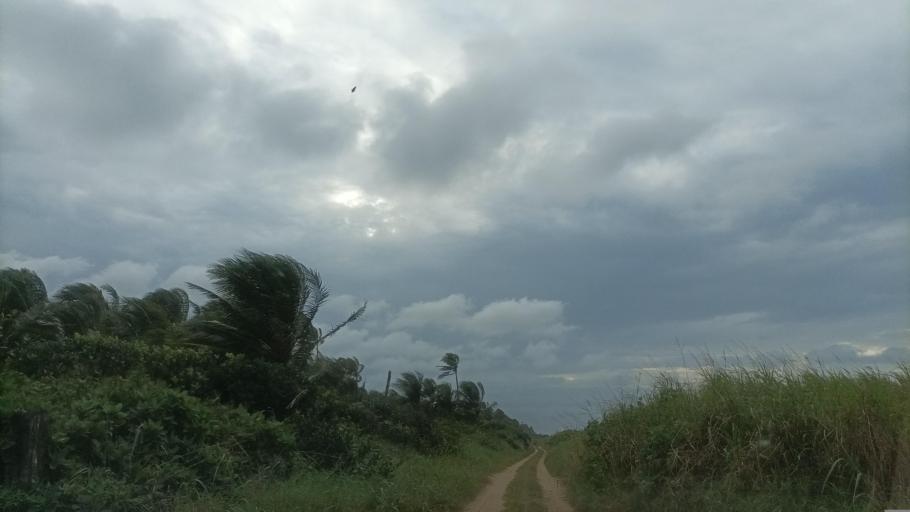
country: MX
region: Veracruz
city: Agua Dulce
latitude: 18.1828
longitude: -94.2601
